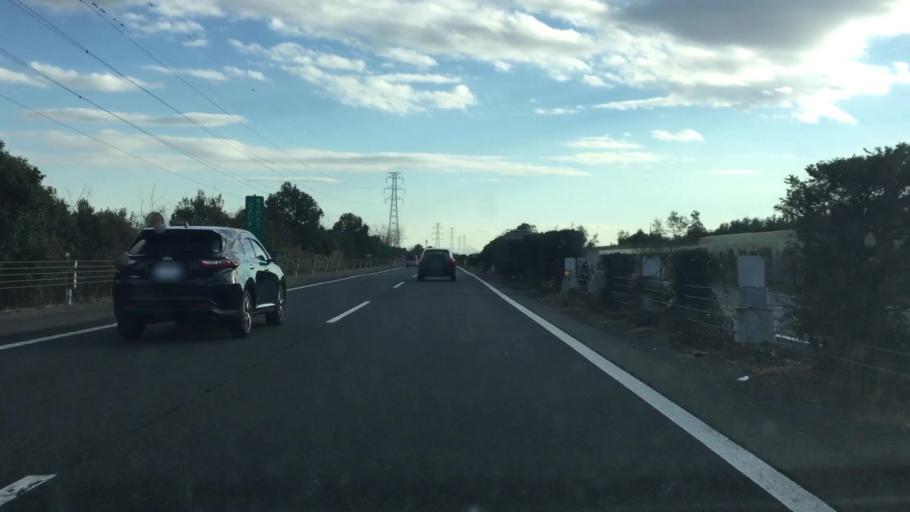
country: JP
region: Gunma
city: Shibukawa
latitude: 36.4583
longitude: 139.0128
